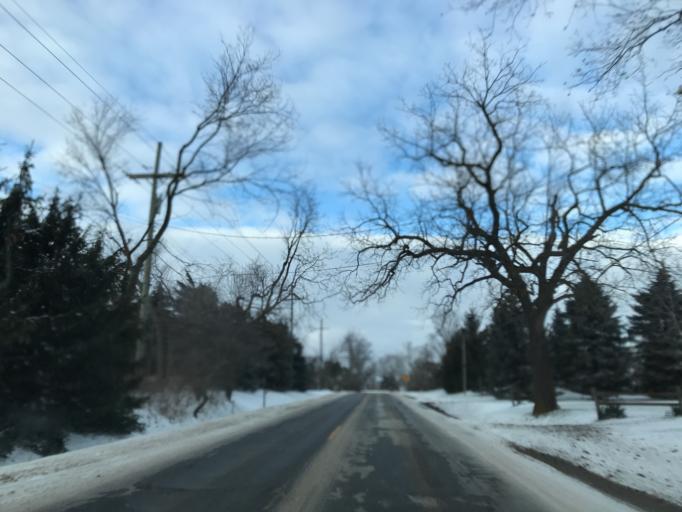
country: US
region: Michigan
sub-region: Oakland County
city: South Lyon
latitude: 42.4306
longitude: -83.5901
